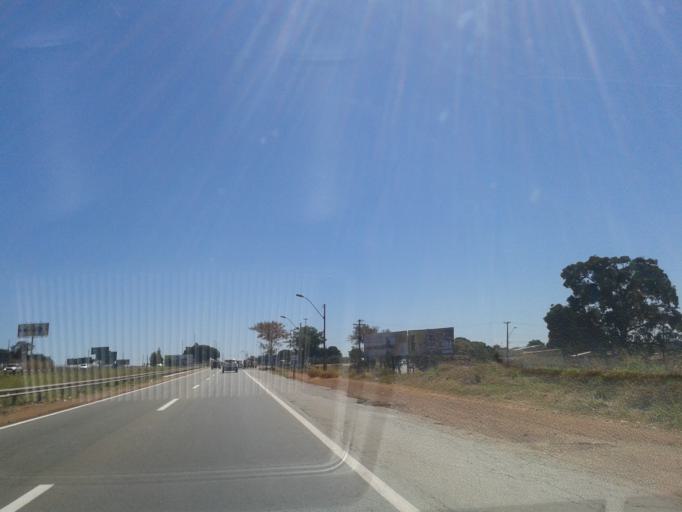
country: BR
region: Goias
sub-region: Goiania
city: Goiania
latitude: -16.6223
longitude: -49.3555
